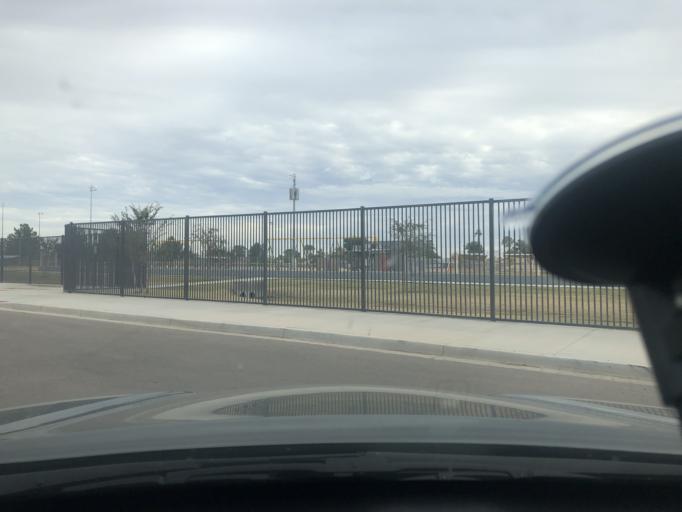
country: US
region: Arizona
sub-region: Maricopa County
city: Scottsdale
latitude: 33.4892
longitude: -111.9004
